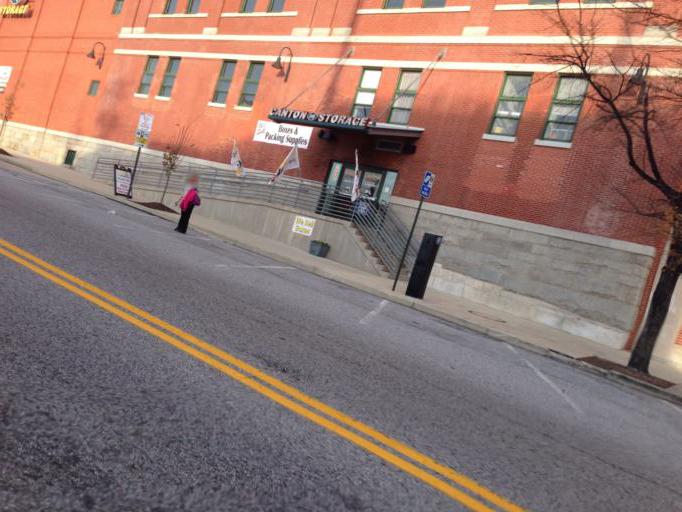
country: US
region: Maryland
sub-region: City of Baltimore
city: Baltimore
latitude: 39.2810
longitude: -76.5671
